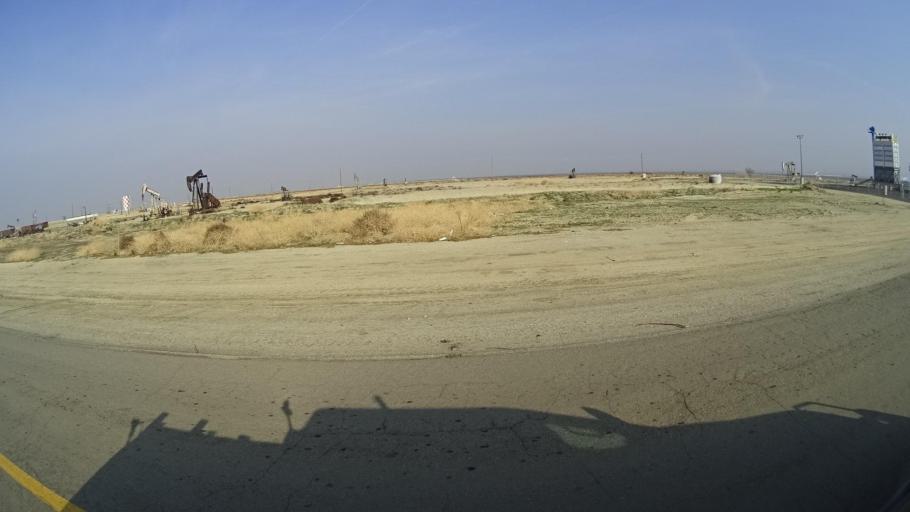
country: US
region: California
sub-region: Kern County
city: Lebec
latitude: 34.9929
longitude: -118.8870
